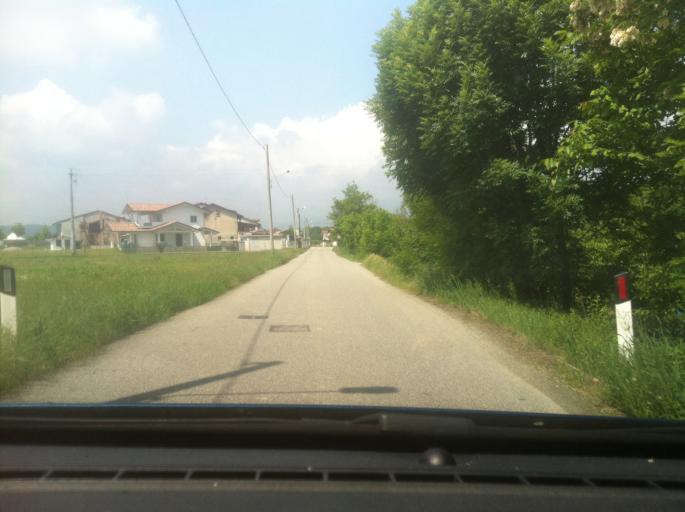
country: IT
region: Piedmont
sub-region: Provincia di Torino
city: Romano Canavese
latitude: 45.4024
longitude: 7.8799
